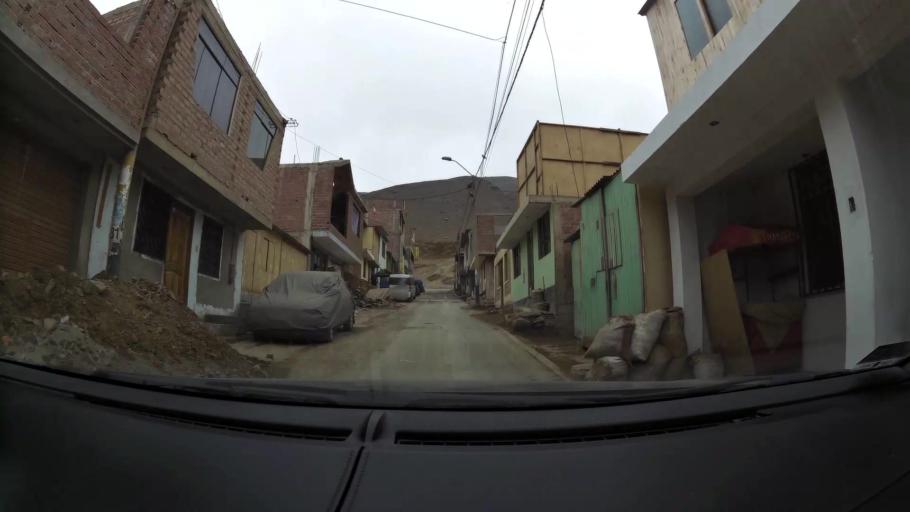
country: PE
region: Lima
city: Ventanilla
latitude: -11.9148
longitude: -77.0930
